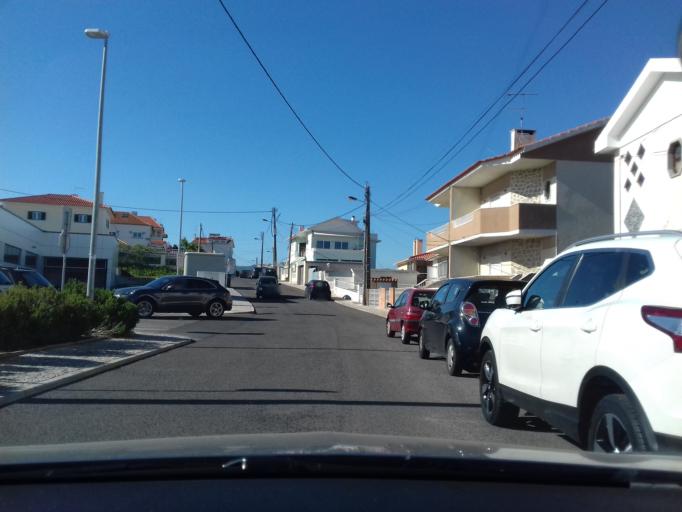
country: PT
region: Lisbon
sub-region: Cascais
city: Alcabideche
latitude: 38.7198
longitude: -9.4096
